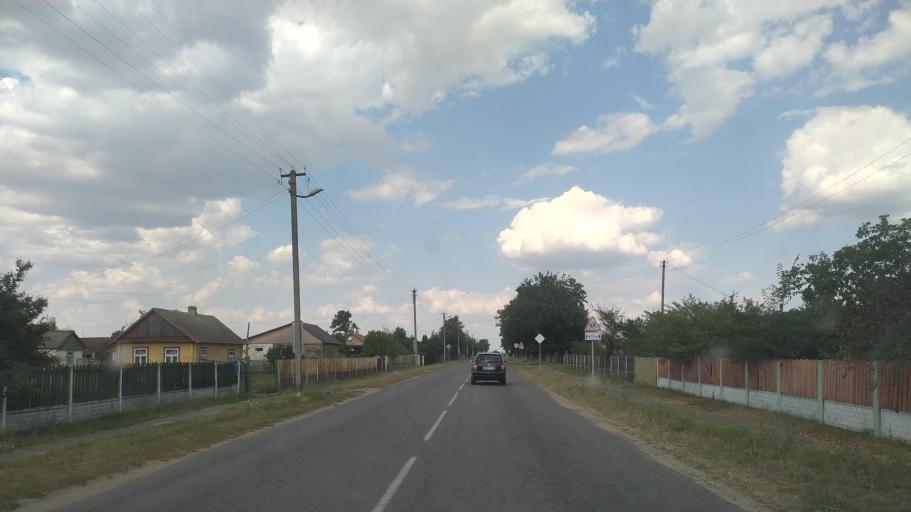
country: BY
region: Brest
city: Drahichyn
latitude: 52.1127
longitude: 25.1152
